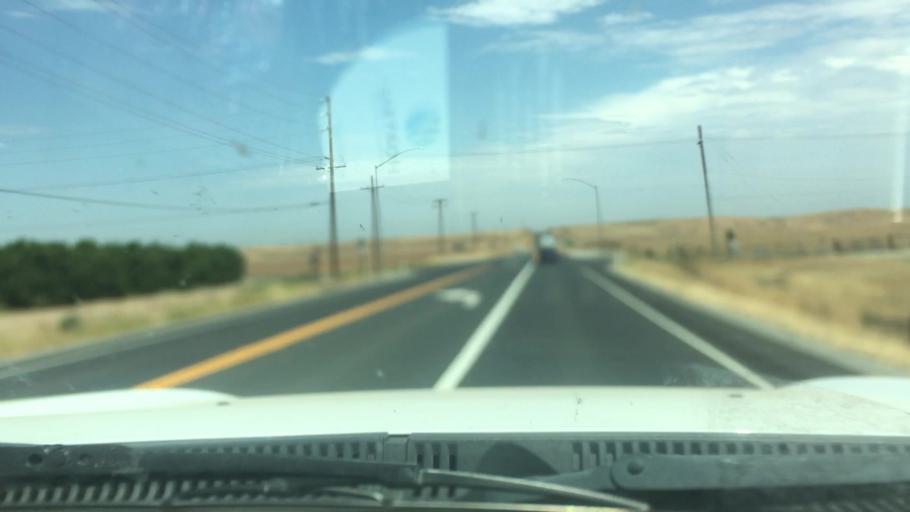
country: US
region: California
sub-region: Tulare County
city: Richgrove
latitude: 35.7612
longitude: -119.0532
